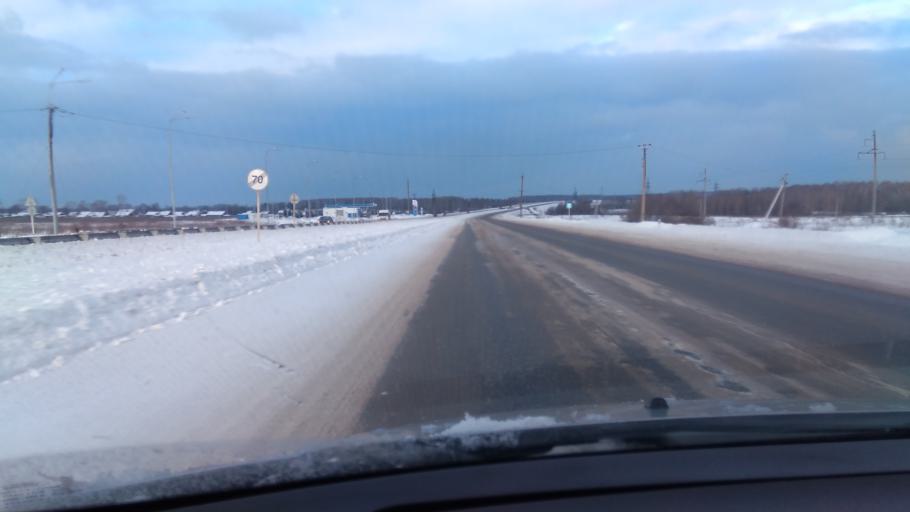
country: RU
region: Sverdlovsk
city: Tsementnyy
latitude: 57.4946
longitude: 60.1761
